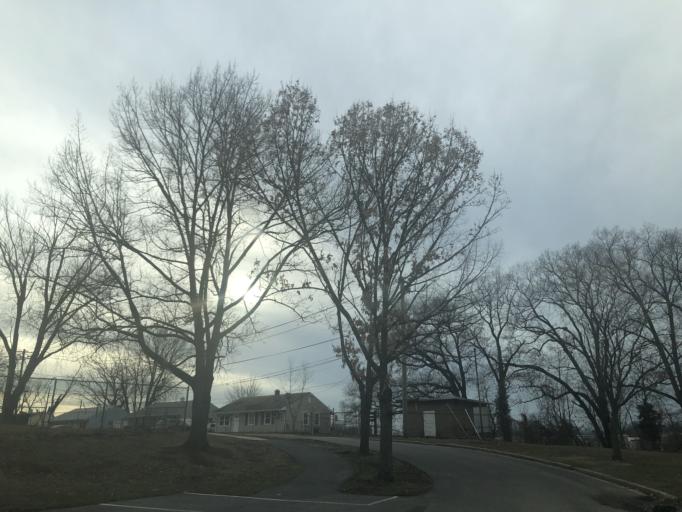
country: US
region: Maryland
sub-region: Prince George's County
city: Oxon Hill
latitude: 38.7958
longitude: -76.9968
